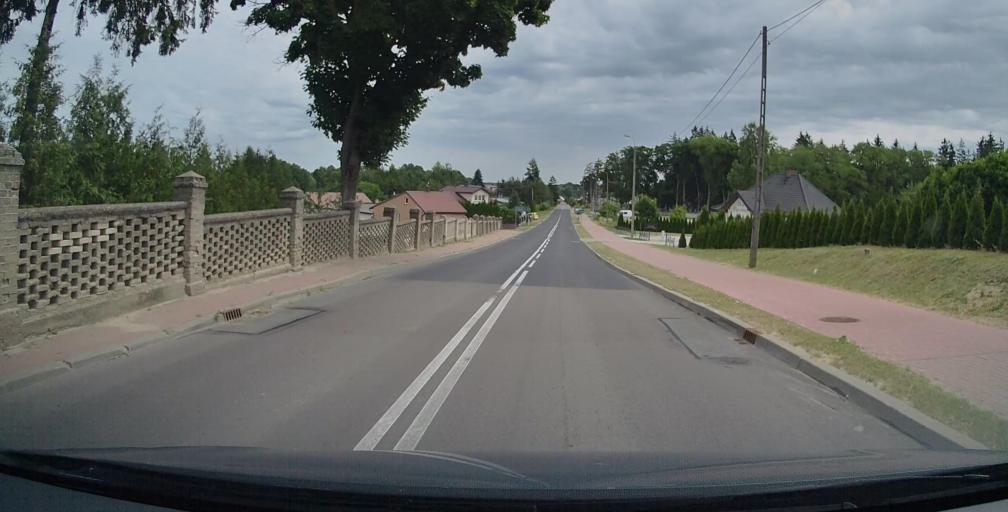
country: PL
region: Masovian Voivodeship
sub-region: Powiat losicki
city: Sarnaki
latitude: 52.3129
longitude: 22.8934
